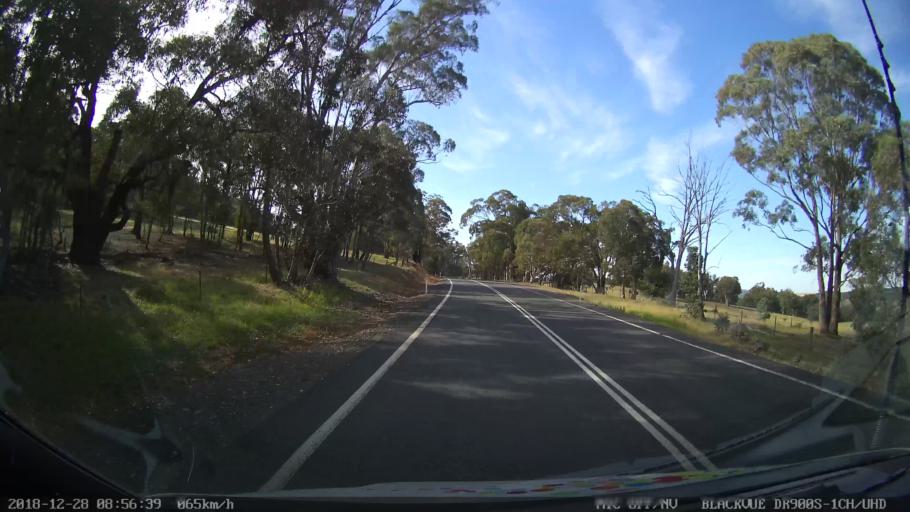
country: AU
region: New South Wales
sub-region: Upper Lachlan Shire
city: Crookwell
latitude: -34.1122
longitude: 149.3378
